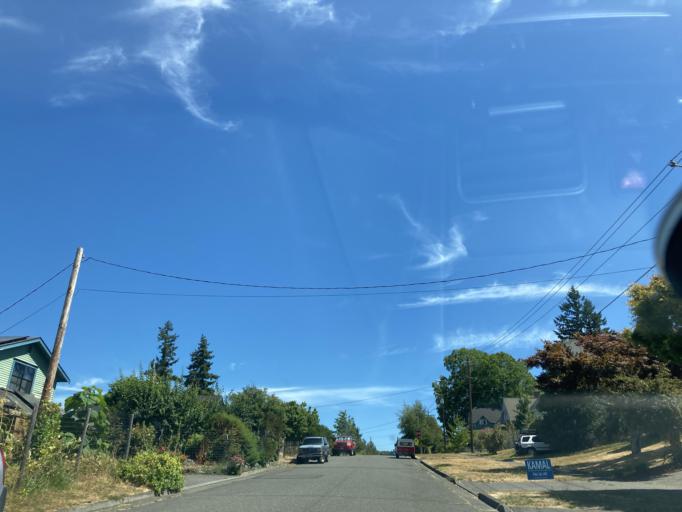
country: US
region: Washington
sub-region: Whatcom County
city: Bellingham
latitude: 48.7193
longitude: -122.4969
